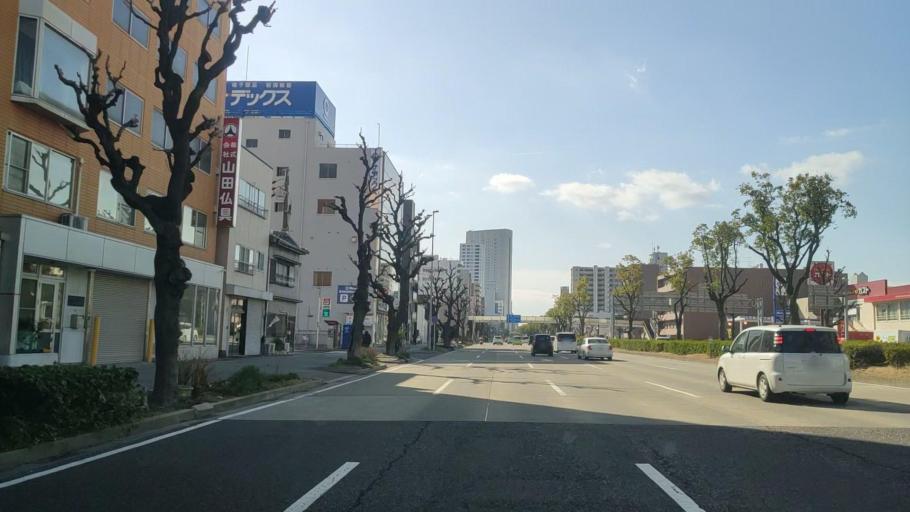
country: JP
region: Aichi
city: Nagoya-shi
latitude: 35.1504
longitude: 136.8991
